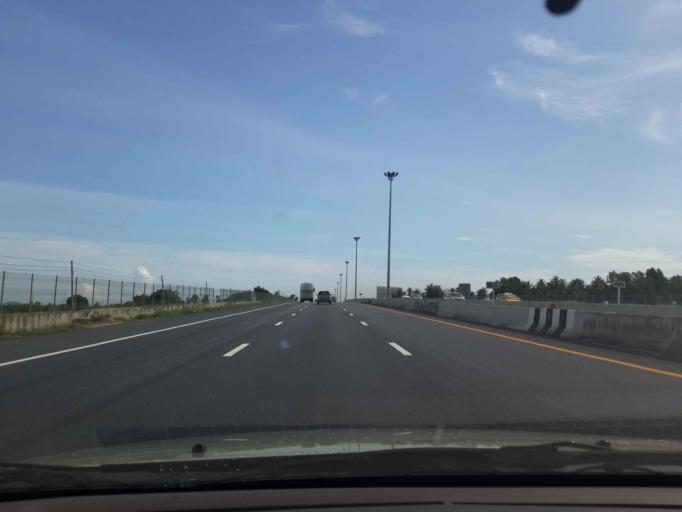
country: TH
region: Chon Buri
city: Ban Talat Bueng
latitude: 13.0290
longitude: 100.9962
